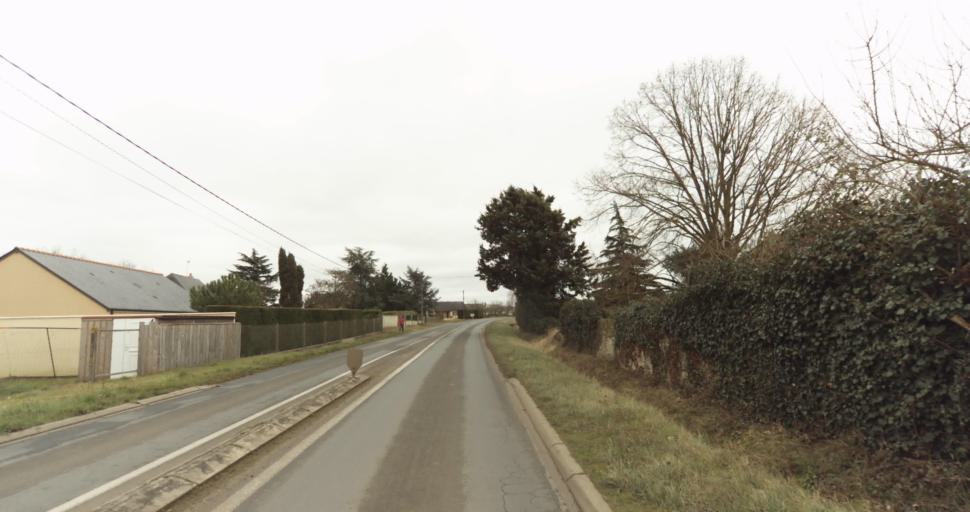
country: FR
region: Pays de la Loire
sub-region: Departement de Maine-et-Loire
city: Doue-la-Fontaine
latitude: 47.1862
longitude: -0.2682
